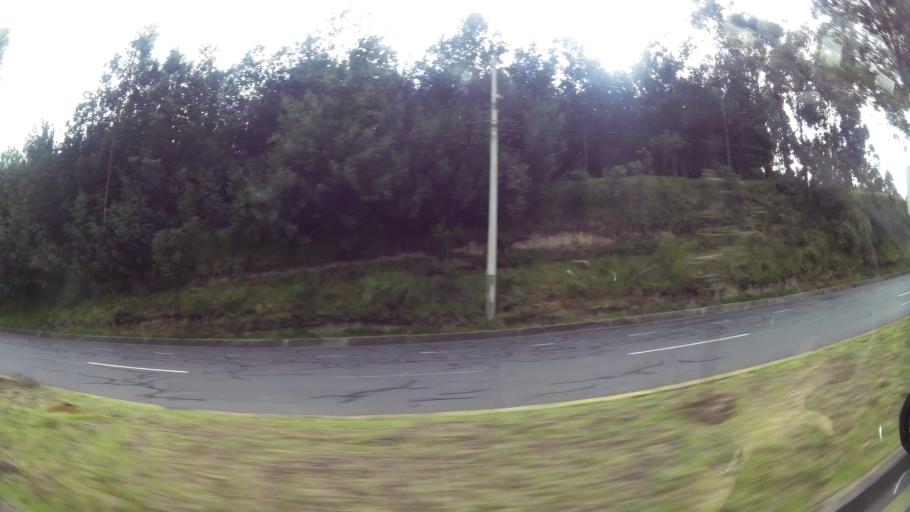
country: EC
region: Pichincha
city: Sangolqui
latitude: -0.3511
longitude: -78.5229
